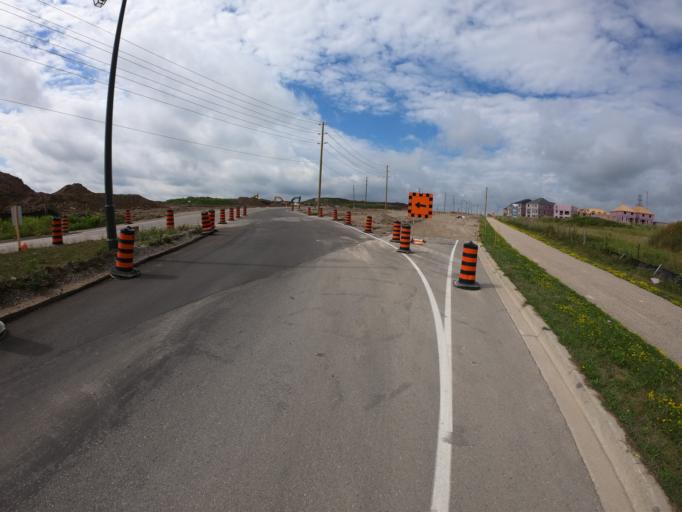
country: CA
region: Ontario
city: Waterloo
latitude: 43.4498
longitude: -80.5854
